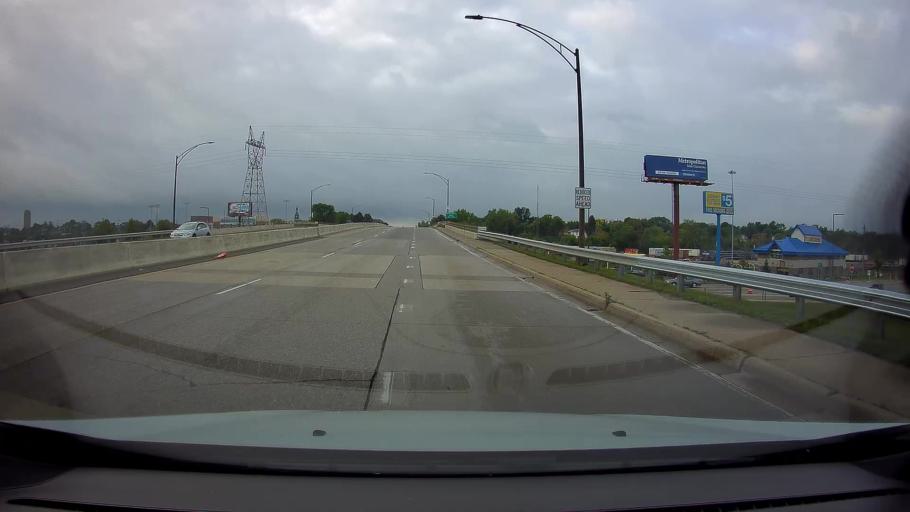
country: US
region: Minnesota
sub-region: Ramsey County
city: Falcon Heights
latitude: 44.9717
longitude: -93.1672
